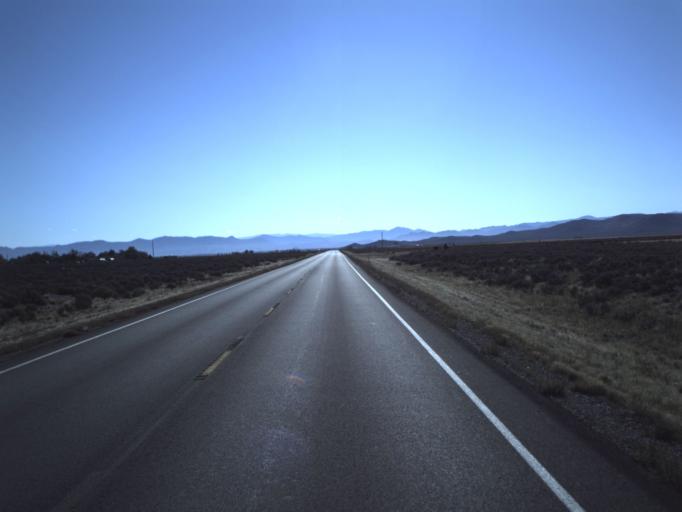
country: US
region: Utah
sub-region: Washington County
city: Enterprise
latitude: 37.7685
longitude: -113.8236
